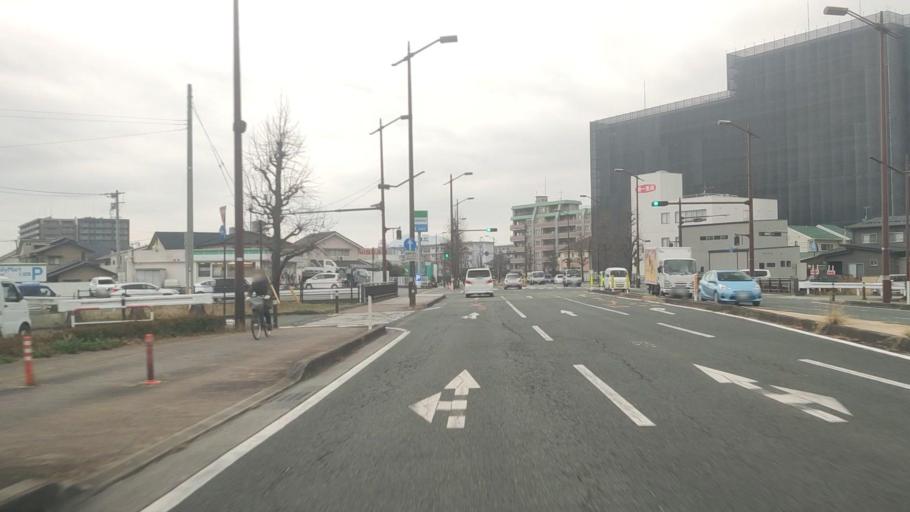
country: JP
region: Kumamoto
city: Kumamoto
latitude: 32.8115
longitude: 130.7767
